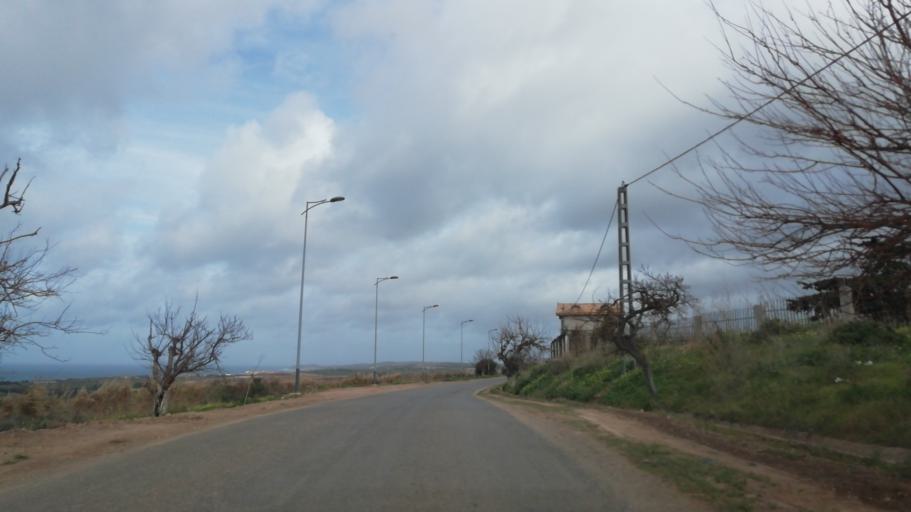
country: DZ
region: Oran
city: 'Ain el Turk
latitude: 35.6917
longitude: -0.8613
